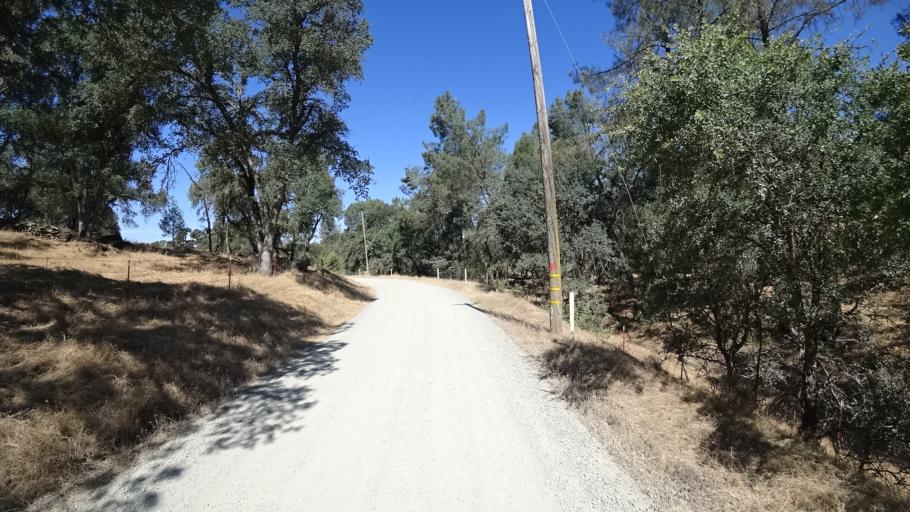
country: US
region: California
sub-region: Calaveras County
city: Valley Springs
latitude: 38.2212
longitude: -120.8826
